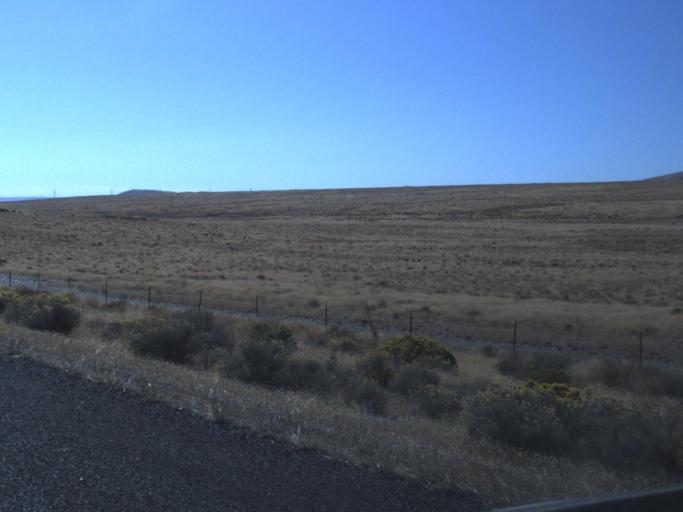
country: US
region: Washington
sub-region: Benton County
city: Benton City
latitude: 46.4261
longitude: -119.4720
